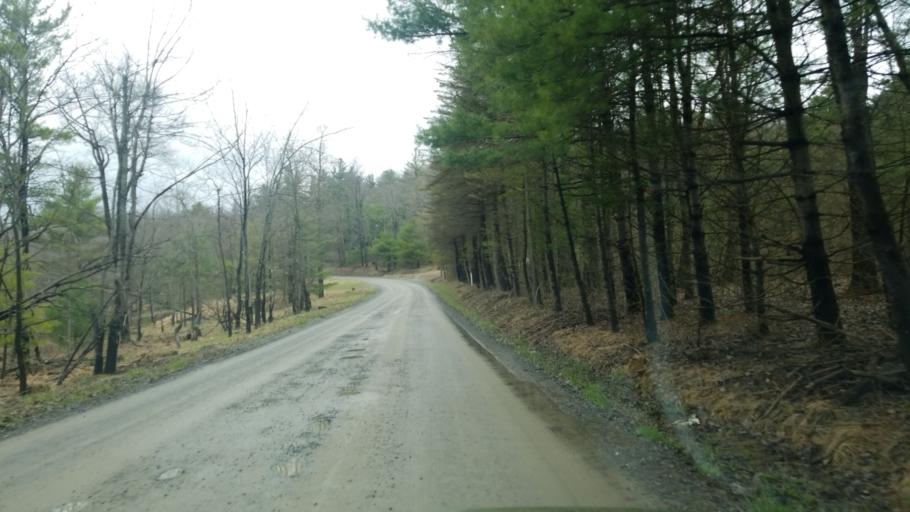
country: US
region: Pennsylvania
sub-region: Clearfield County
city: Shiloh
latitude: 41.1440
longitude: -78.3376
